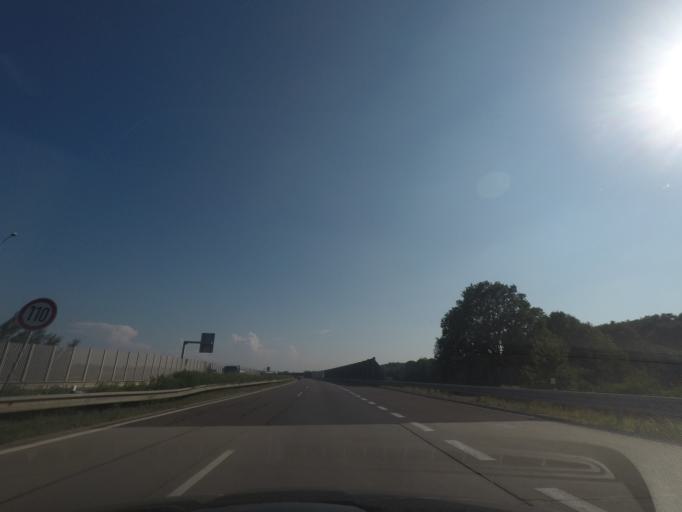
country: PL
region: Silesian Voivodeship
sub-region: Powiat raciborski
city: Chalupki
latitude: 49.9006
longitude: 18.3047
